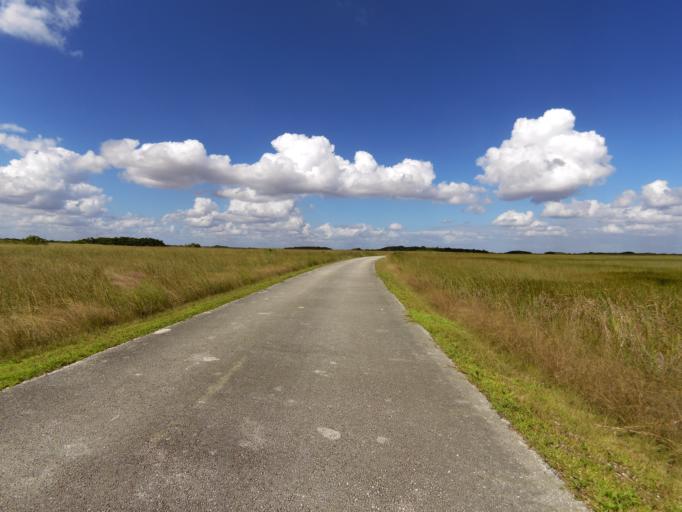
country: US
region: Florida
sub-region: Miami-Dade County
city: The Hammocks
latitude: 25.6670
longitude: -80.7614
